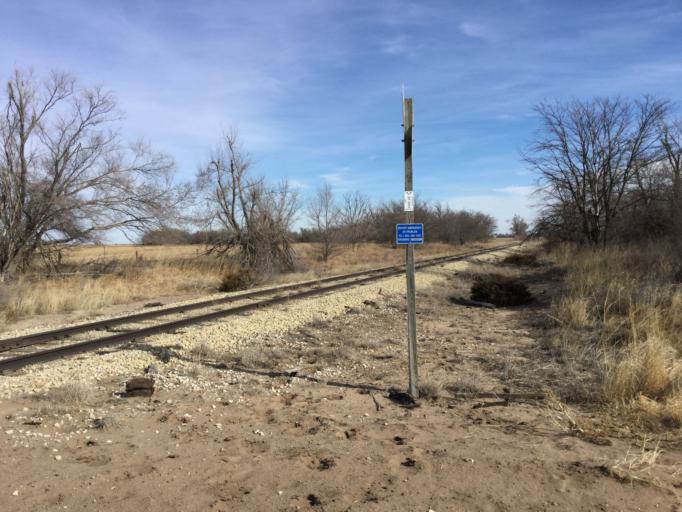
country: US
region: Kansas
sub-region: Rice County
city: Sterling
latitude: 38.2613
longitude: -98.3694
